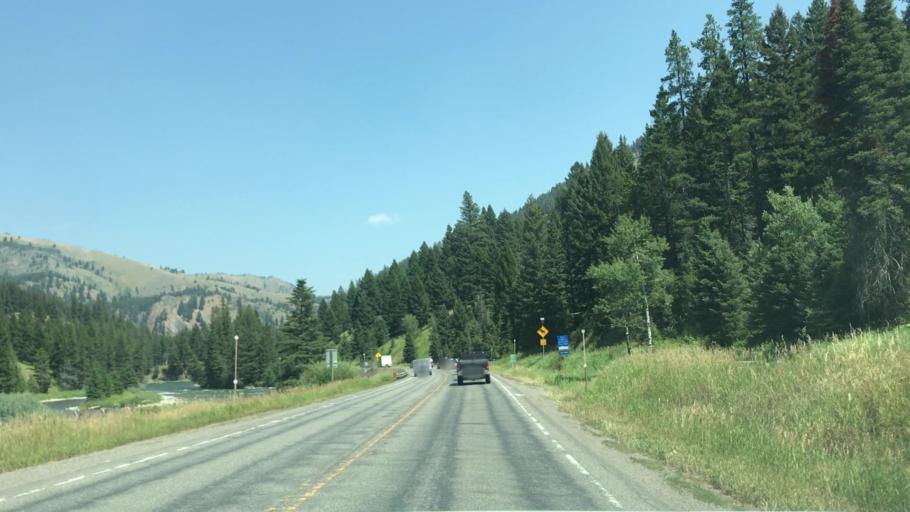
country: US
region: Montana
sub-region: Gallatin County
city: Big Sky
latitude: 45.2836
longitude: -111.2240
